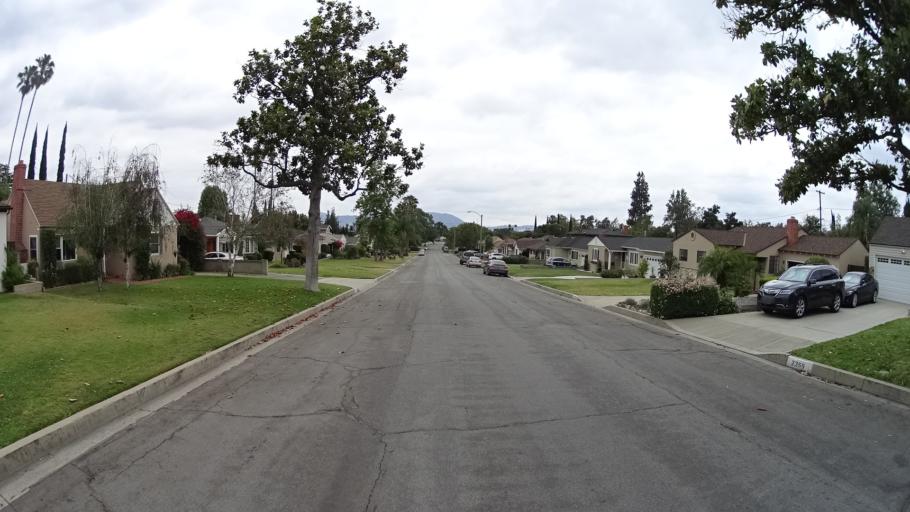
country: US
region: California
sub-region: Los Angeles County
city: Burbank
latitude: 34.2017
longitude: -118.3285
